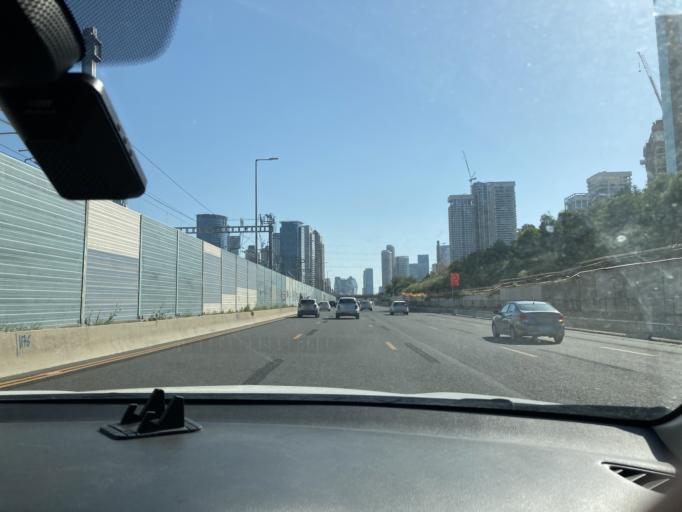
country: IL
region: Tel Aviv
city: Ramat Gan
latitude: 32.0946
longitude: 34.8013
